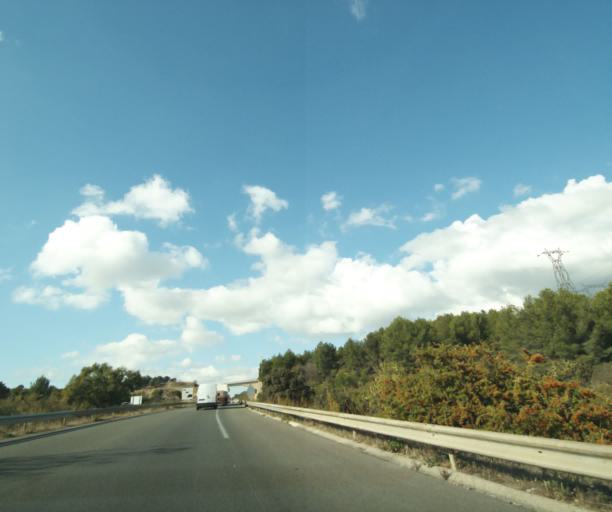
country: FR
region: Provence-Alpes-Cote d'Azur
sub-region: Departement des Bouches-du-Rhone
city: Septemes-les-Vallons
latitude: 43.4007
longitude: 5.3491
